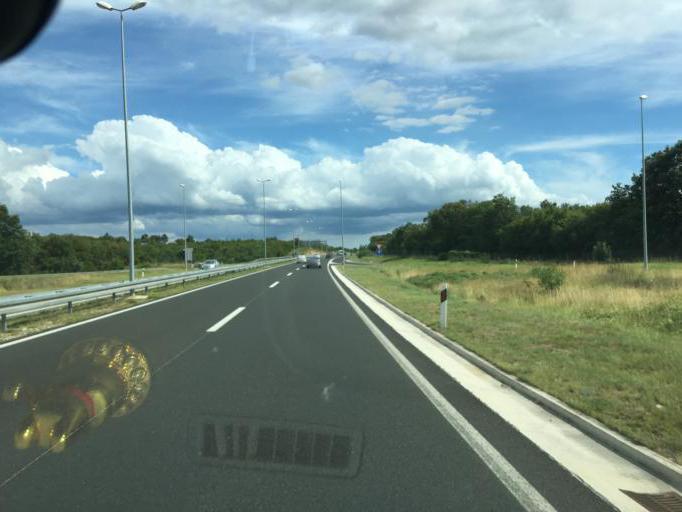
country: HR
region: Istarska
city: Vodnjan
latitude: 45.1102
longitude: 13.8159
